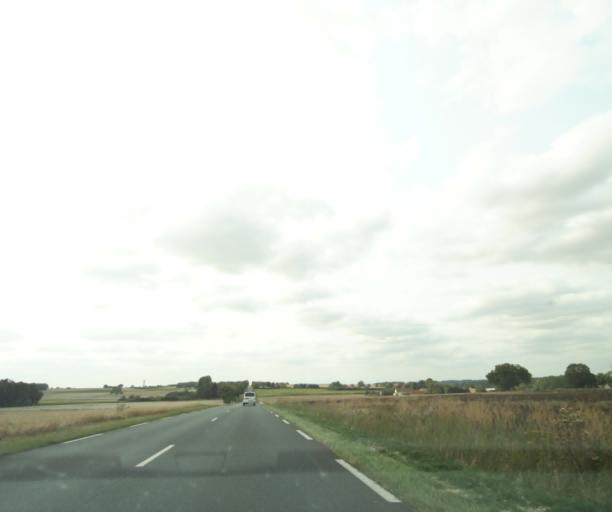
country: FR
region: Centre
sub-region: Departement de l'Indre
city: Clion
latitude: 46.9289
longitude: 1.2755
